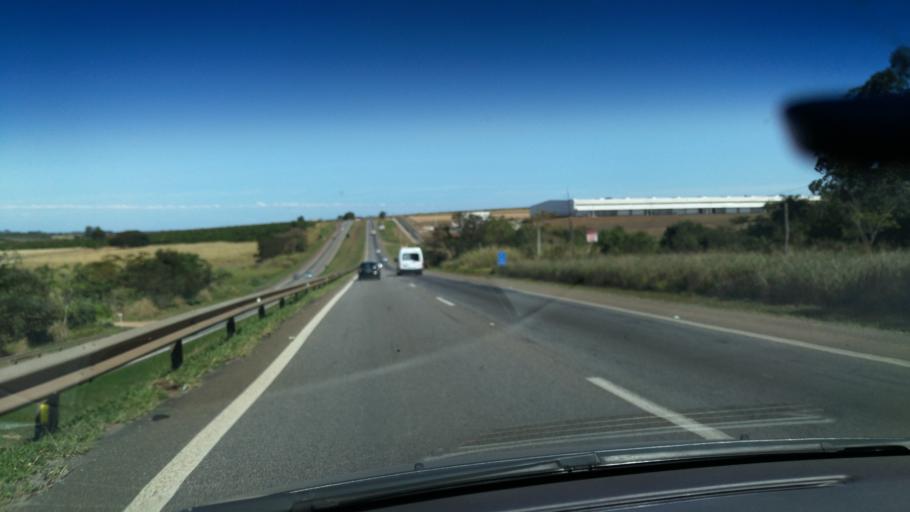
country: BR
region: Sao Paulo
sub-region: Santo Antonio De Posse
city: Santo Antonio de Posse
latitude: -22.5383
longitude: -46.9963
